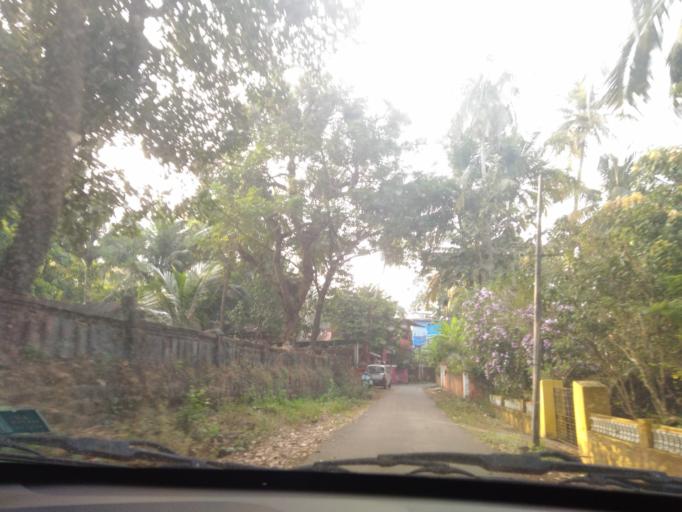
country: IN
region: Goa
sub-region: South Goa
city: Cuncolim
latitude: 15.1787
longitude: 73.9698
